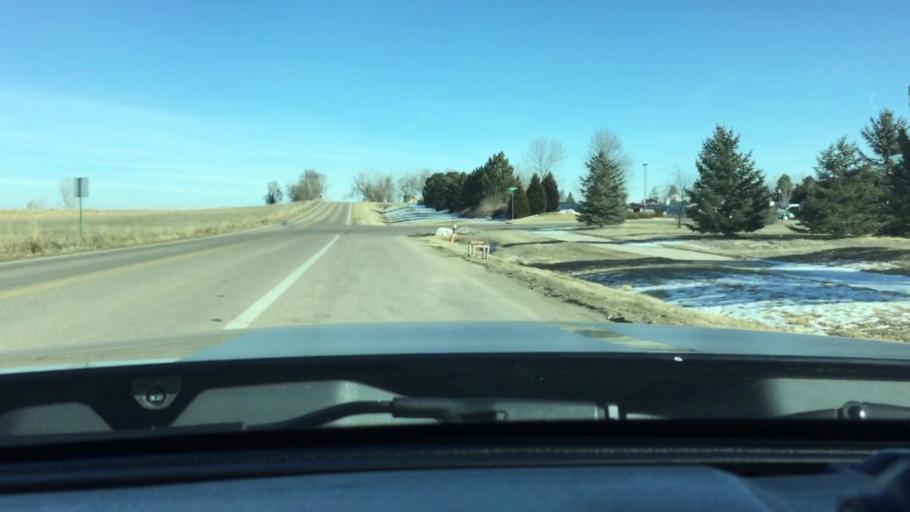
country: US
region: Colorado
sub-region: Weld County
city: Johnstown
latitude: 40.3636
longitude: -104.9779
